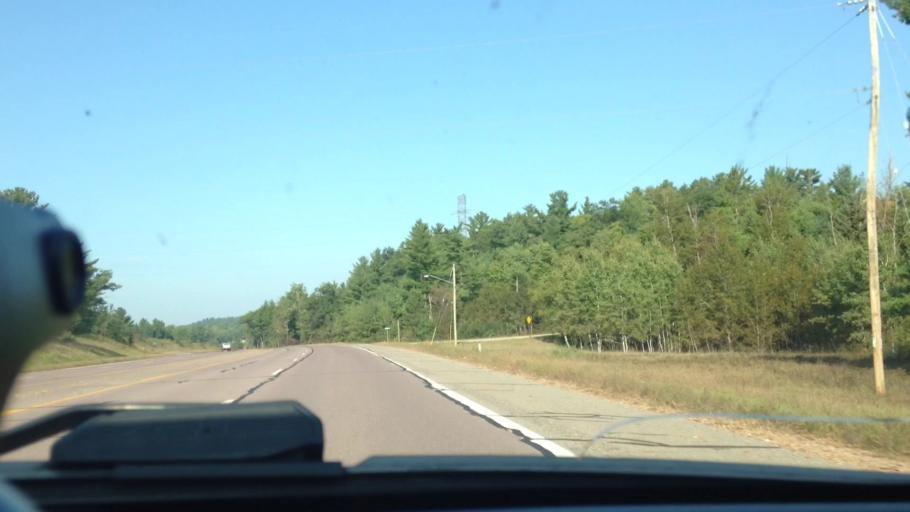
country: US
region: Michigan
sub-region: Dickinson County
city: Quinnesec
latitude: 45.8040
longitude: -87.9680
